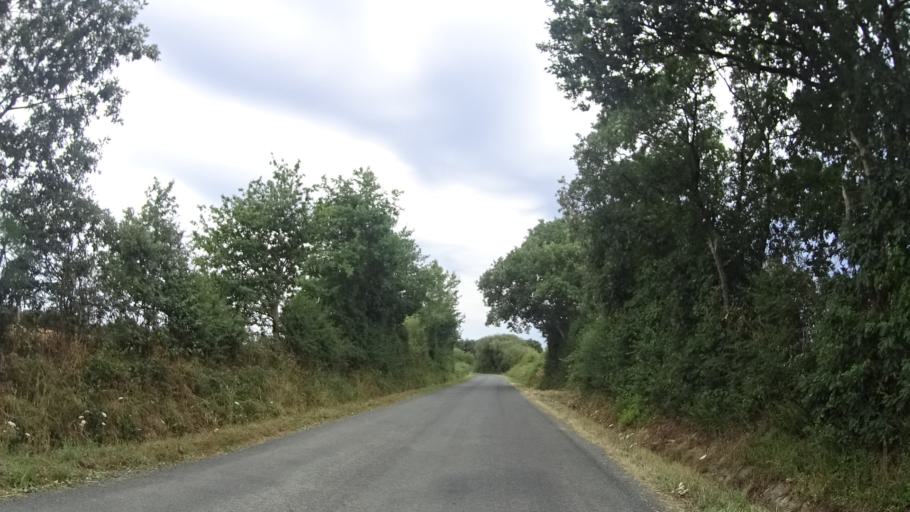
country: FR
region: Pays de la Loire
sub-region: Departement de la Loire-Atlantique
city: Fay-de-Bretagne
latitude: 47.4248
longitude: -1.7533
